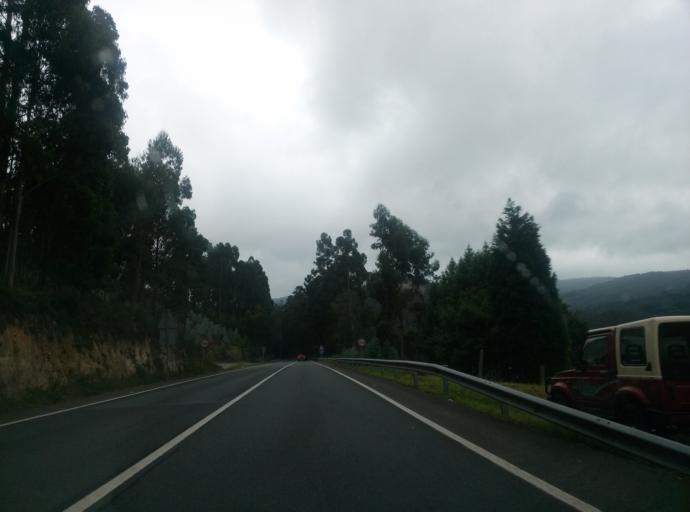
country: ES
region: Galicia
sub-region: Provincia de Lugo
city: Viveiro
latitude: 43.6084
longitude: -7.6058
